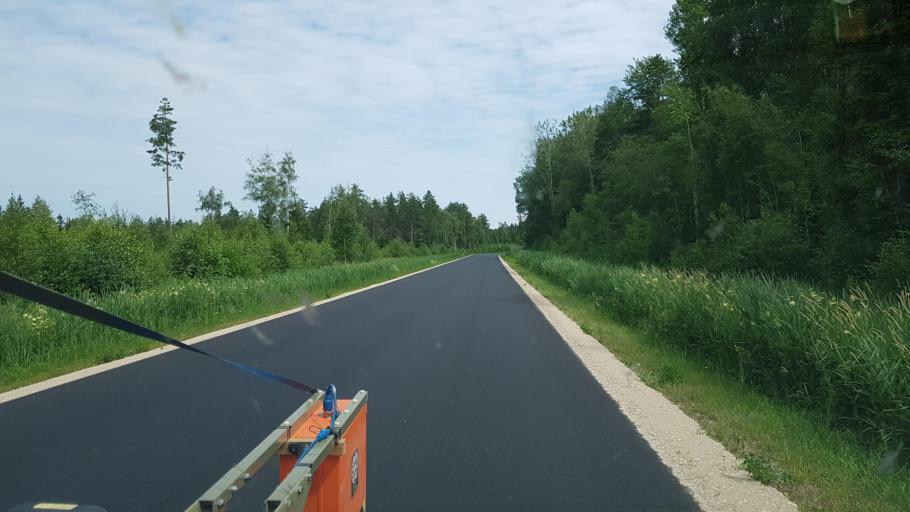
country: EE
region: Paernumaa
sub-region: Audru vald
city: Audru
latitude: 58.6178
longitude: 24.2294
